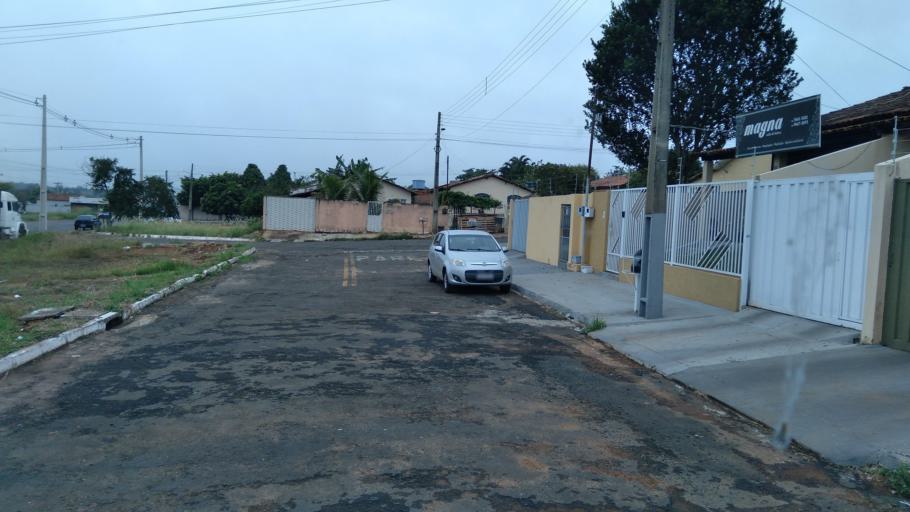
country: BR
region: Goias
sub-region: Mineiros
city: Mineiros
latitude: -17.5720
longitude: -52.5392
